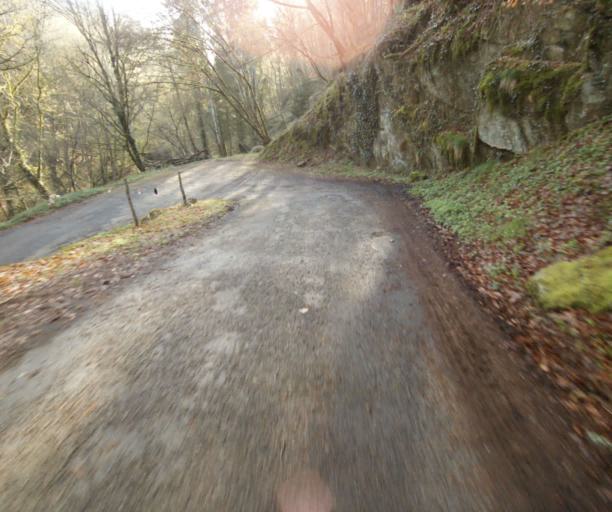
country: FR
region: Limousin
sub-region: Departement de la Correze
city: Correze
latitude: 45.3009
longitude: 1.8532
